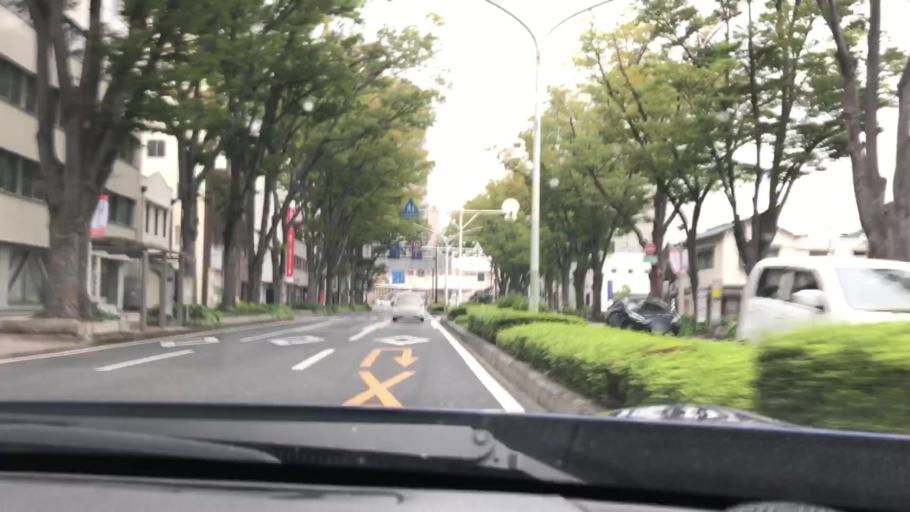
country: JP
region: Gunma
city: Maebashi-shi
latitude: 36.3870
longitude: 139.0726
